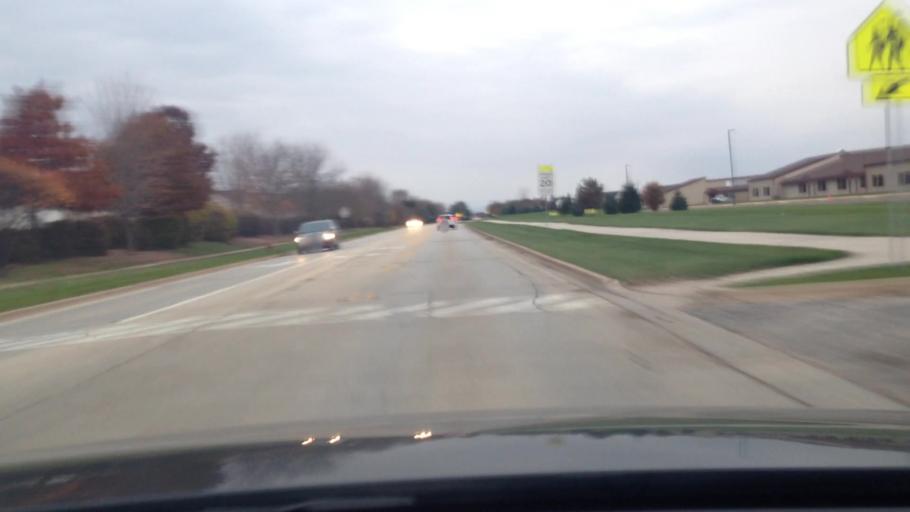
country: US
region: Illinois
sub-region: McHenry County
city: Huntley
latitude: 42.1828
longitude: -88.4077
